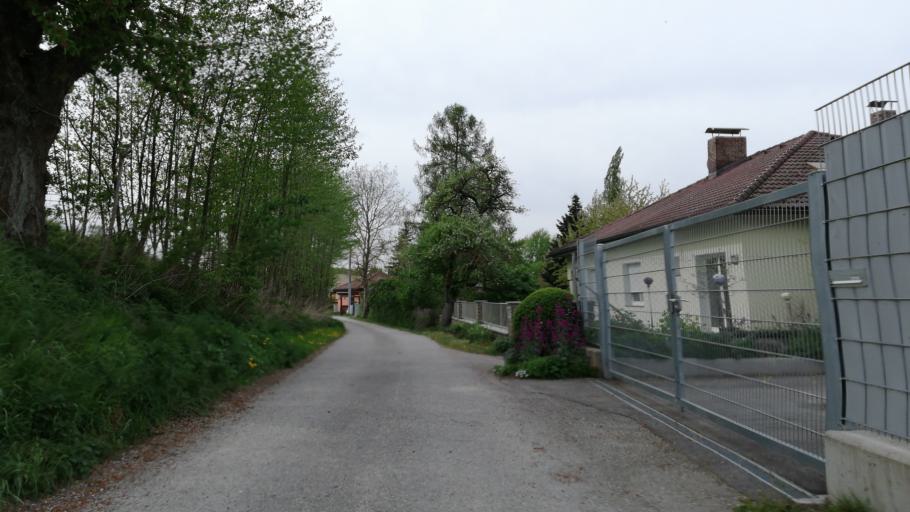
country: AT
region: Upper Austria
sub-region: Politischer Bezirk Grieskirchen
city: Bad Schallerbach
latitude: 48.1863
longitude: 13.9459
